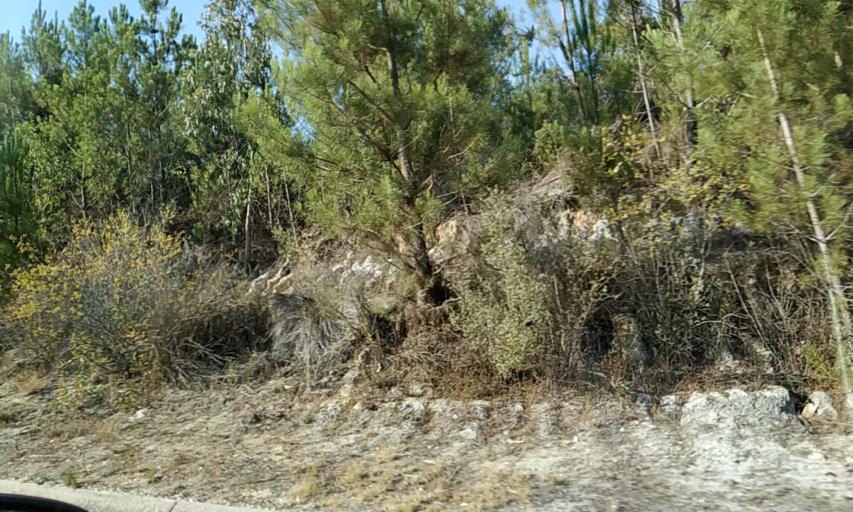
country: PT
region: Santarem
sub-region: Almeirim
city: Fazendas de Almeirim
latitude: 39.1158
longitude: -8.5864
